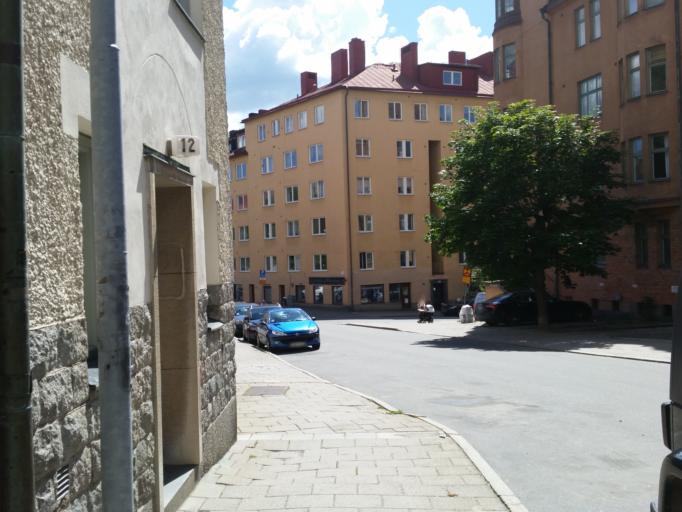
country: SE
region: Stockholm
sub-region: Solna Kommun
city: Solna
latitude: 59.3649
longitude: 17.9965
